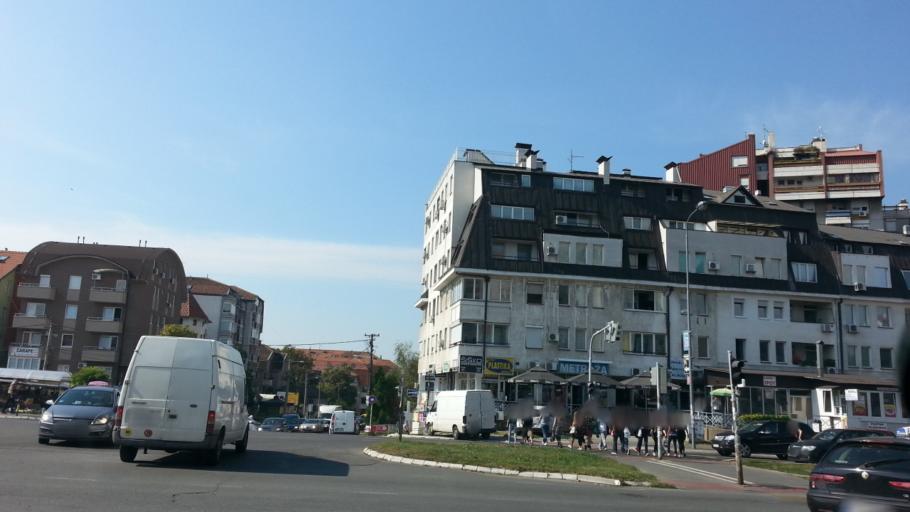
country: RS
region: Central Serbia
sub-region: Belgrade
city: Cukarica
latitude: 44.7592
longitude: 20.4155
